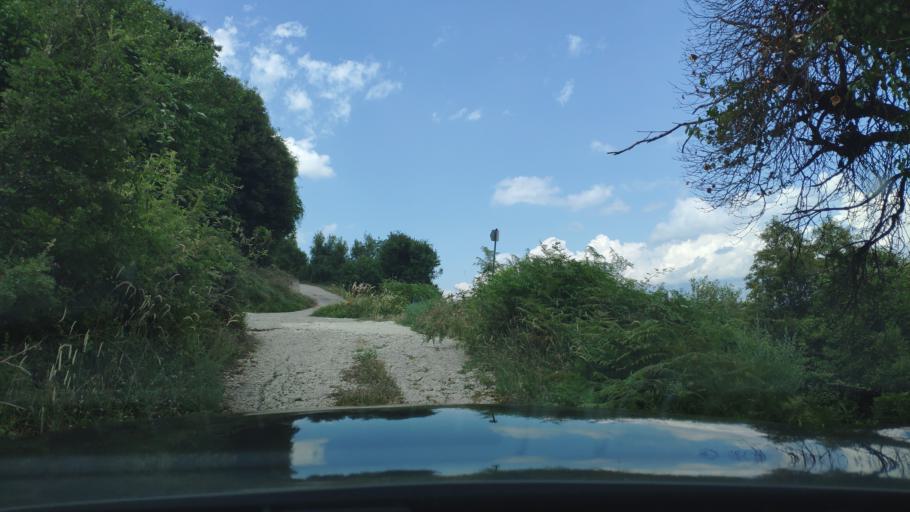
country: GR
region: Epirus
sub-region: Nomos Artas
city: Agios Dimitrios
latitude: 39.3202
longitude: 20.9996
